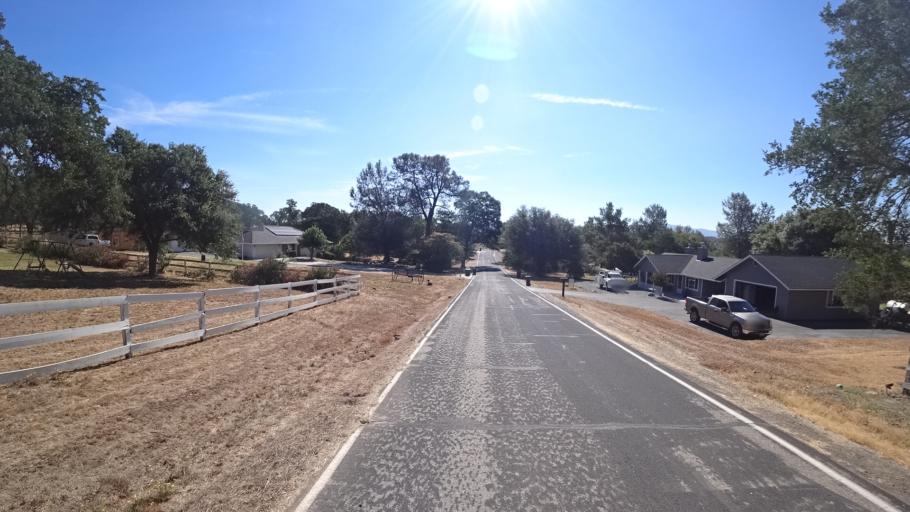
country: US
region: California
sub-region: Calaveras County
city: Valley Springs
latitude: 38.1704
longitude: -120.8556
